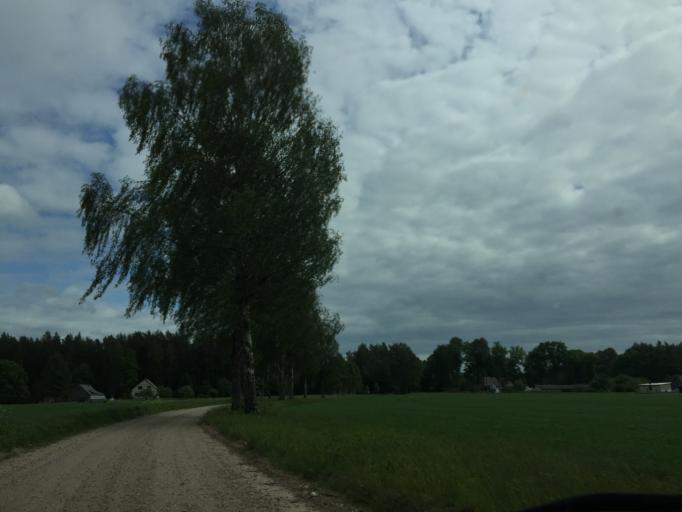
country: LV
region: Valmieras Rajons
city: Valmiera
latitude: 57.5786
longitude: 25.5104
